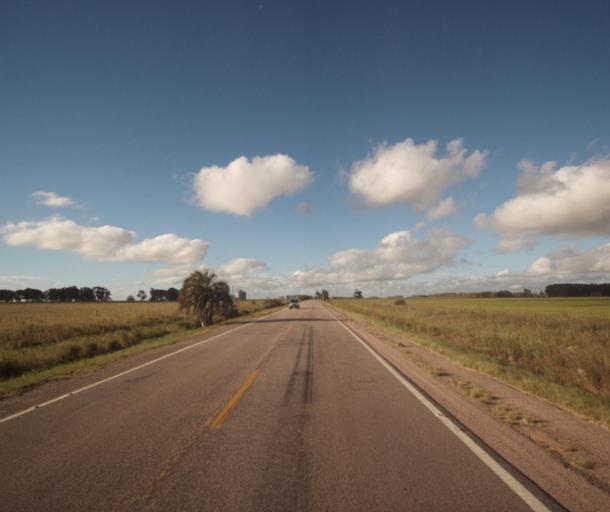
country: BR
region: Rio Grande do Sul
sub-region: Arroio Grande
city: Arroio Grande
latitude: -32.4492
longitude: -52.5701
